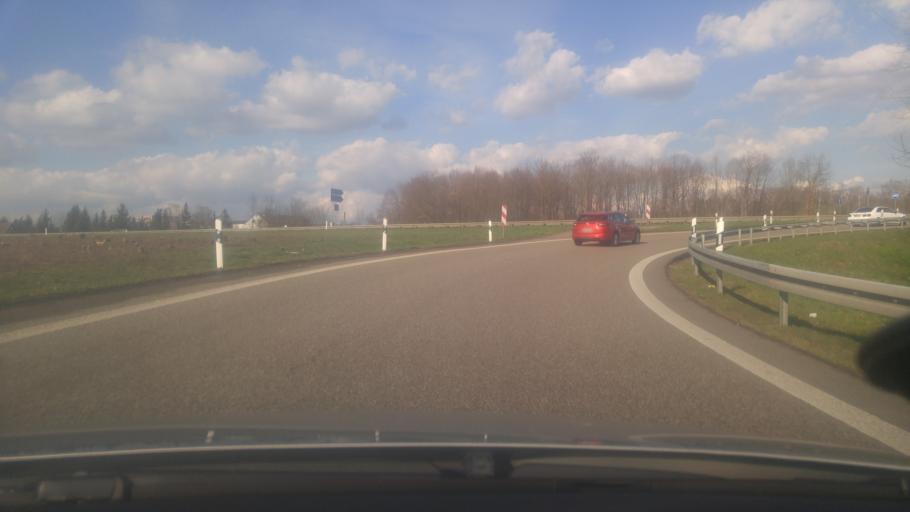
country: DE
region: Baden-Wuerttemberg
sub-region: Regierungsbezirk Stuttgart
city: Korntal
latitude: 48.8511
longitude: 9.1188
